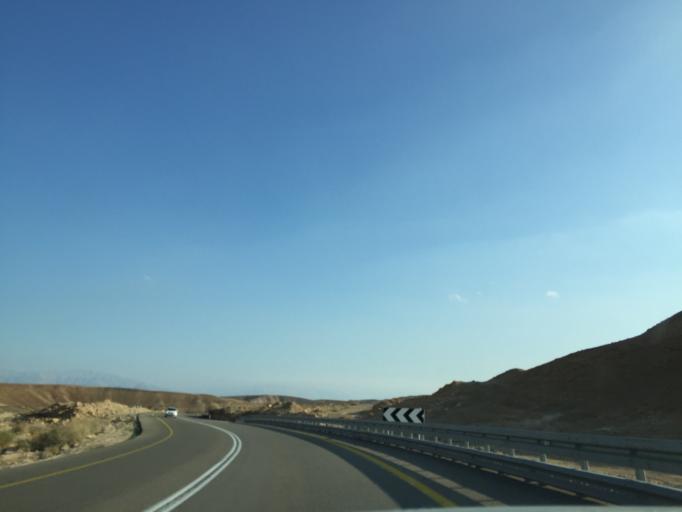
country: IL
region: Southern District
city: `En Boqeq
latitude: 31.1799
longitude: 35.2938
